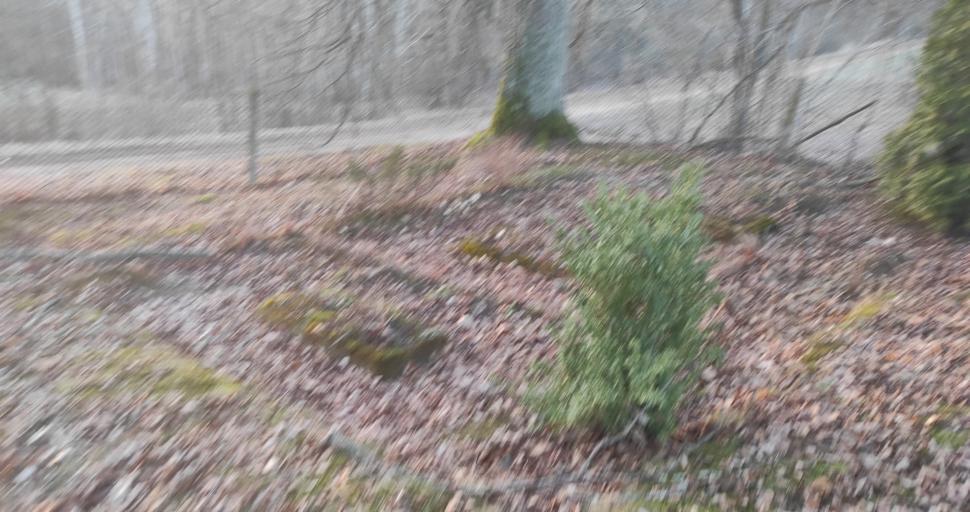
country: LV
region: Aizpute
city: Aizpute
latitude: 56.8054
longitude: 21.8052
